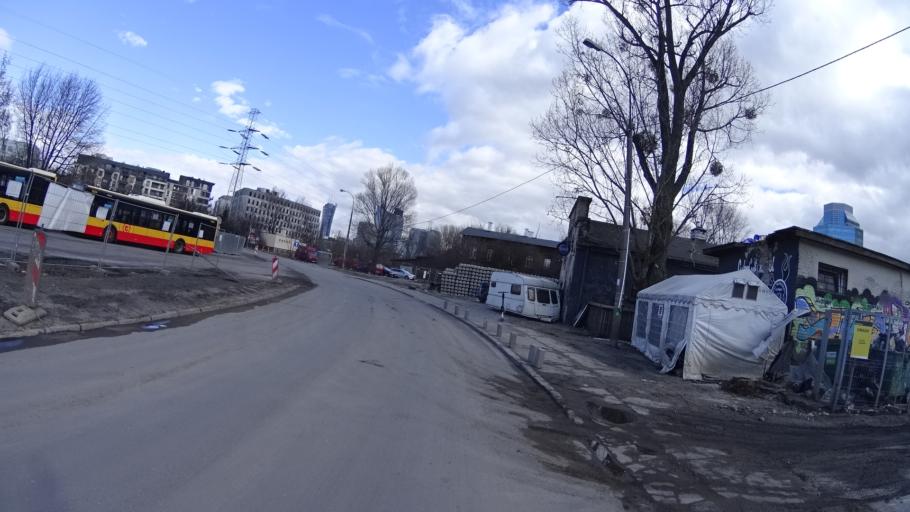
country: PL
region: Masovian Voivodeship
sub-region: Warszawa
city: Ochota
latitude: 52.2218
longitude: 20.9685
